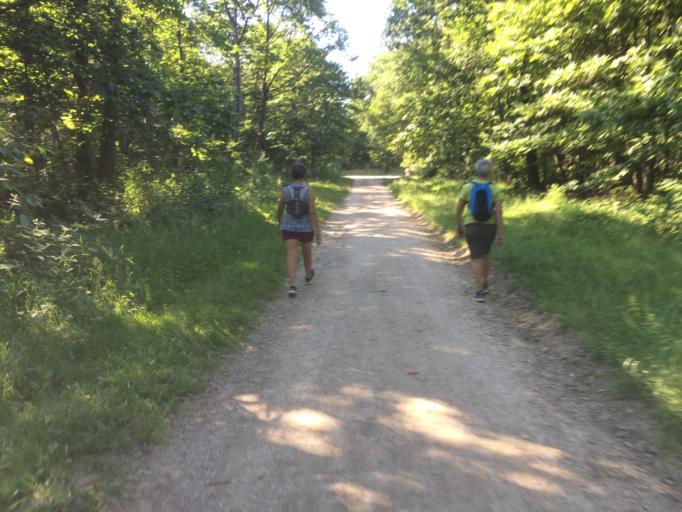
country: FR
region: Ile-de-France
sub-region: Departement du Val-de-Marne
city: Sucy-en-Brie
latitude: 48.7526
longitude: 2.5485
